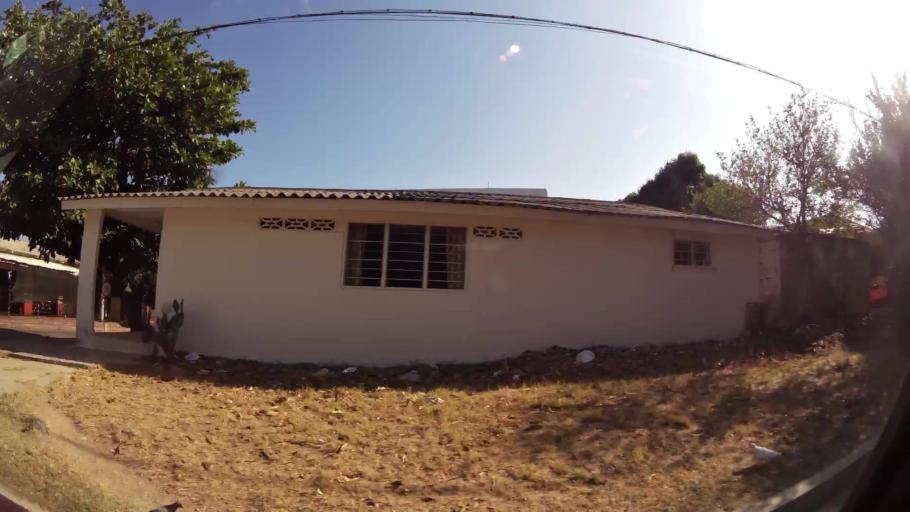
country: CO
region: Atlantico
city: Barranquilla
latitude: 11.0234
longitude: -74.8039
